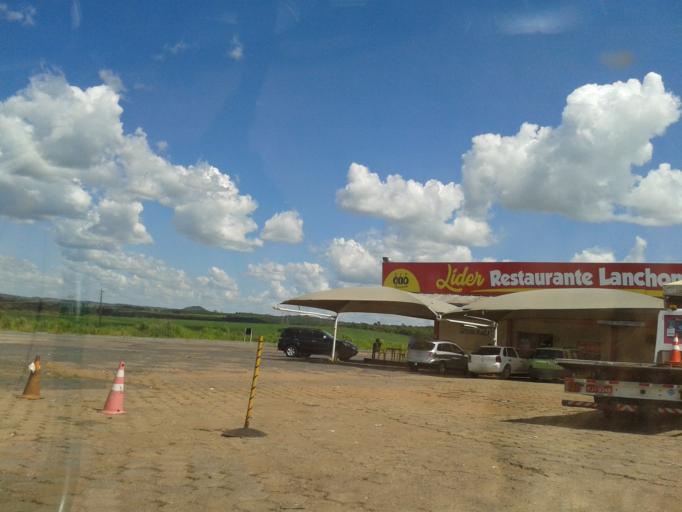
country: BR
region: Goias
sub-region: Pontalina
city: Pontalina
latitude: -17.5279
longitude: -49.2157
